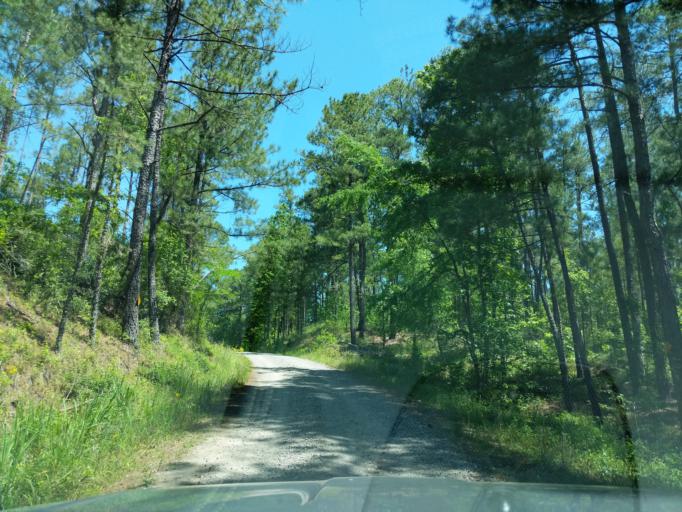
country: US
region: Georgia
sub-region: Columbia County
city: Evans
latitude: 33.6155
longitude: -82.1141
